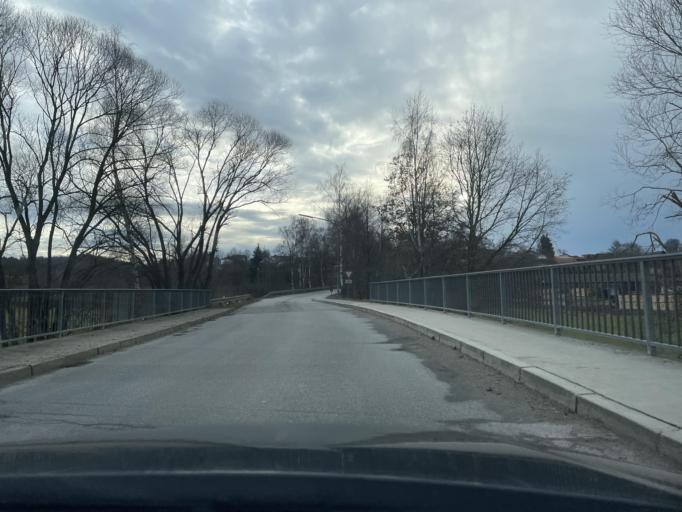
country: DE
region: Bavaria
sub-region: Lower Bavaria
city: Ruhmannsfelden
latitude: 48.9881
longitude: 12.9910
